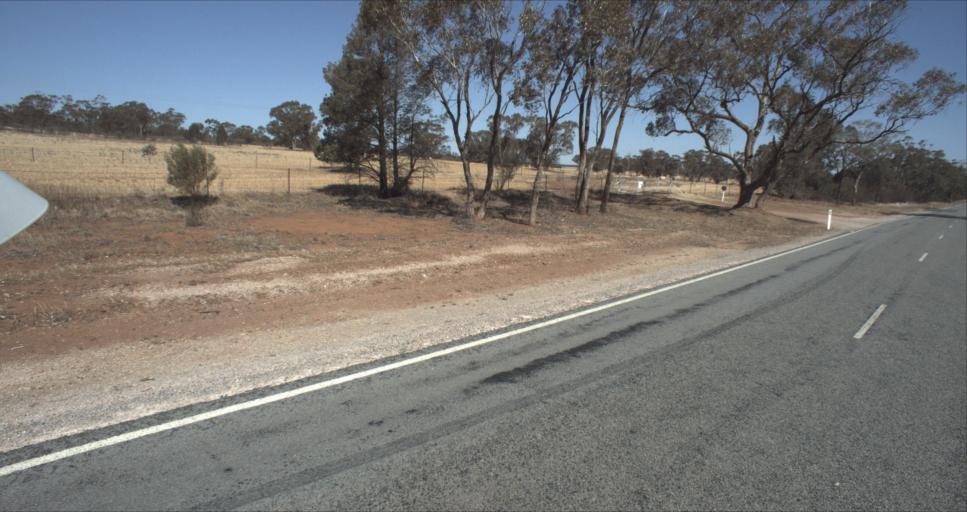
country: AU
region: New South Wales
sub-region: Leeton
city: Leeton
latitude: -34.4792
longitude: 146.4345
